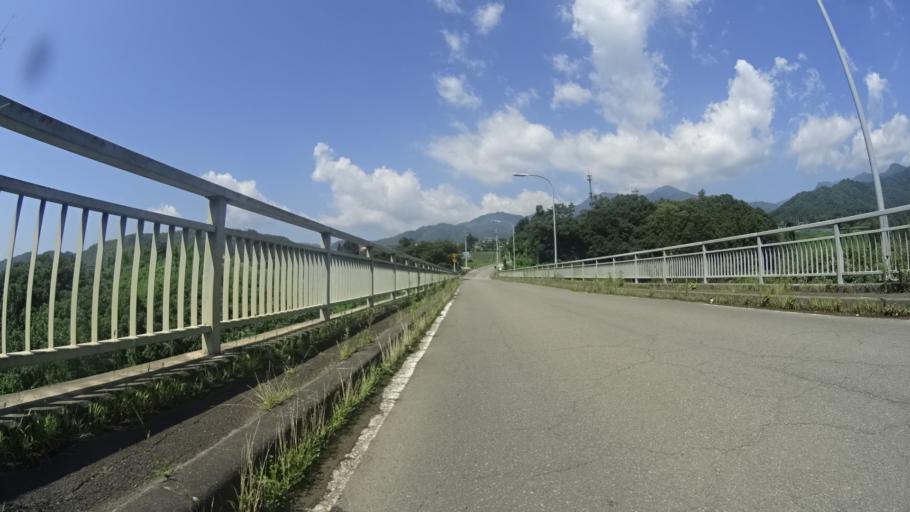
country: JP
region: Yamanashi
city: Enzan
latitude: 35.7441
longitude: 138.7216
